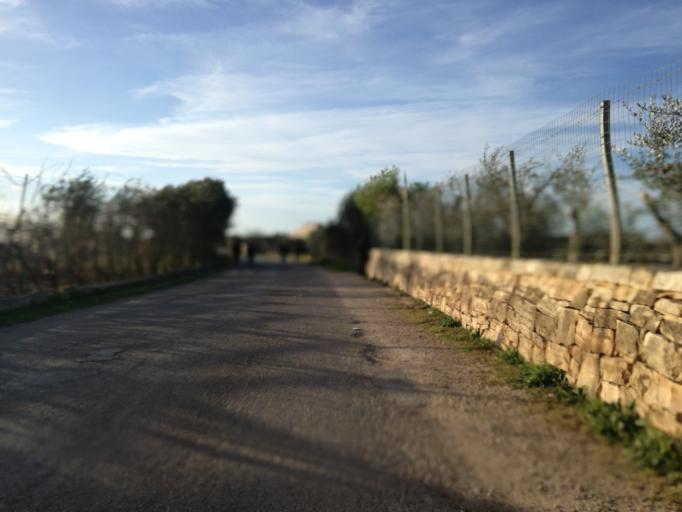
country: IT
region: Apulia
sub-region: Provincia di Bari
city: Valenzano
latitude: 41.0513
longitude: 16.8997
